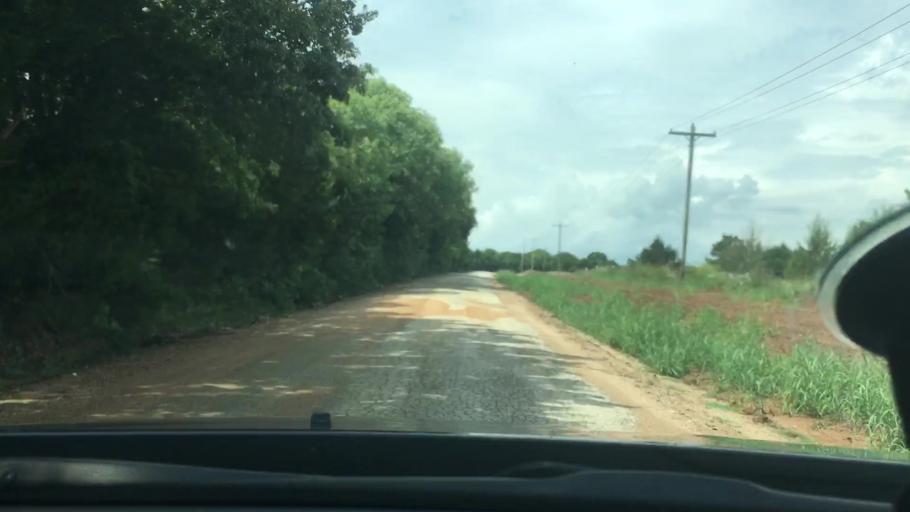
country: US
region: Oklahoma
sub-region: Carter County
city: Dickson
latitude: 34.2454
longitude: -96.9246
